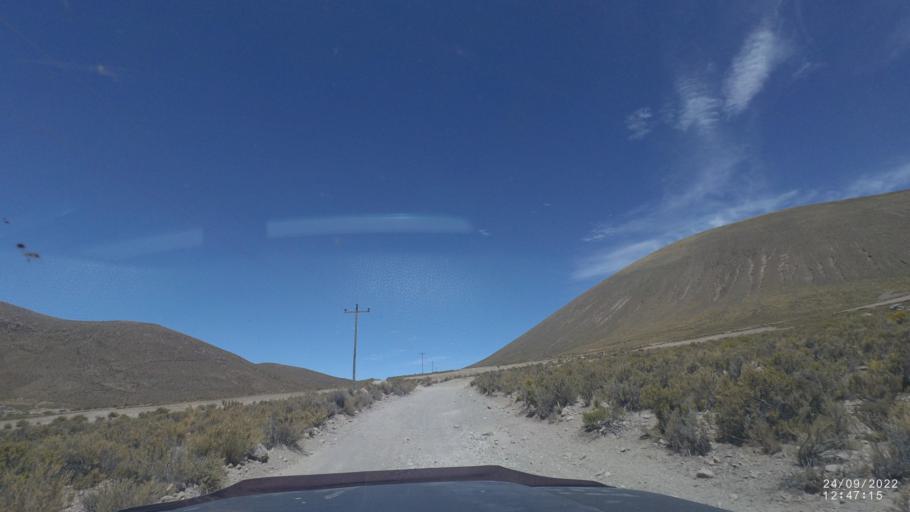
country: BO
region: Potosi
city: Colchani
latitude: -19.8083
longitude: -67.5687
